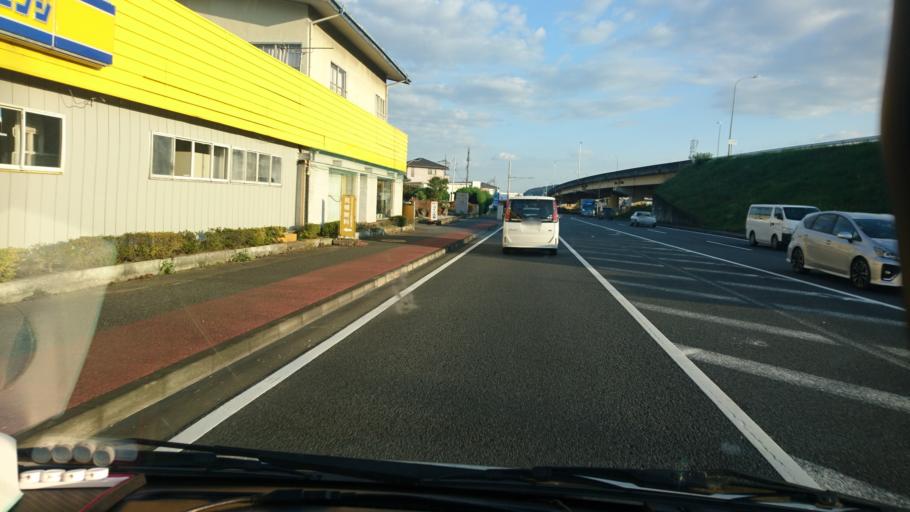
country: JP
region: Gunma
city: Kiryu
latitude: 36.3863
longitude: 139.3355
